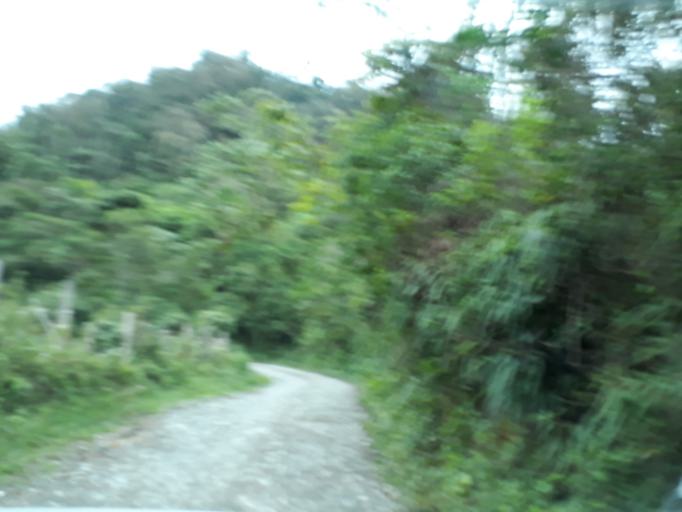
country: CO
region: Boyaca
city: Muzo
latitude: 5.3803
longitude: -74.0747
